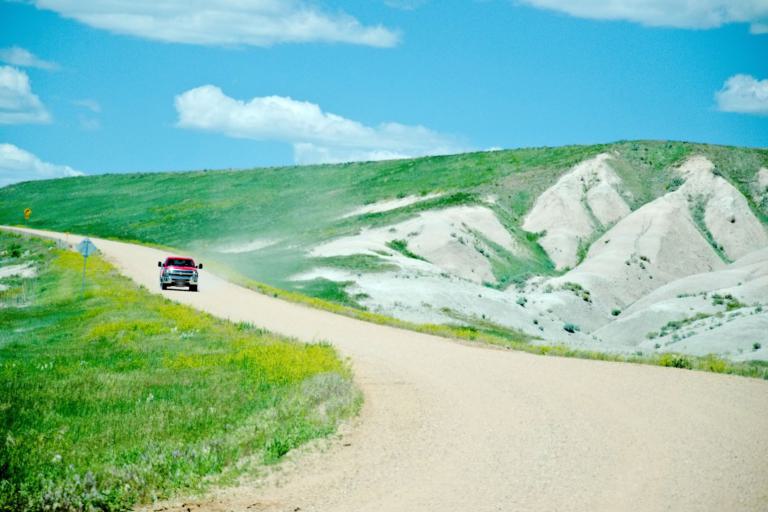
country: US
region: South Dakota
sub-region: Shannon County
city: Porcupine
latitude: 43.8016
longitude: -102.5098
